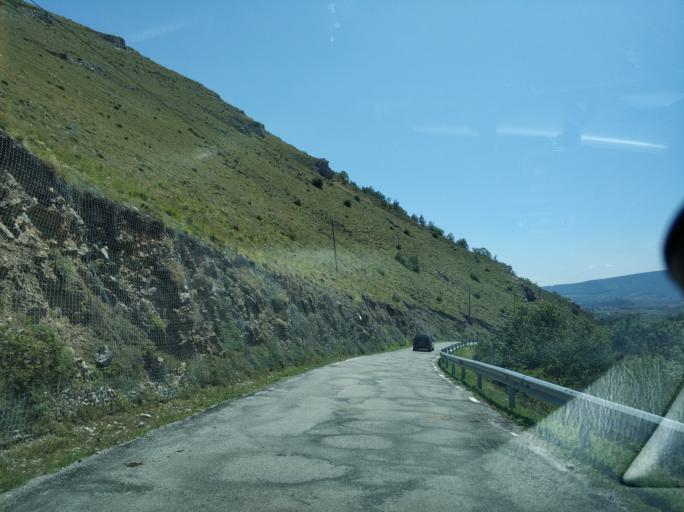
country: ES
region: Cantabria
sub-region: Provincia de Cantabria
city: Reinosa
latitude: 43.0288
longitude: -4.1690
